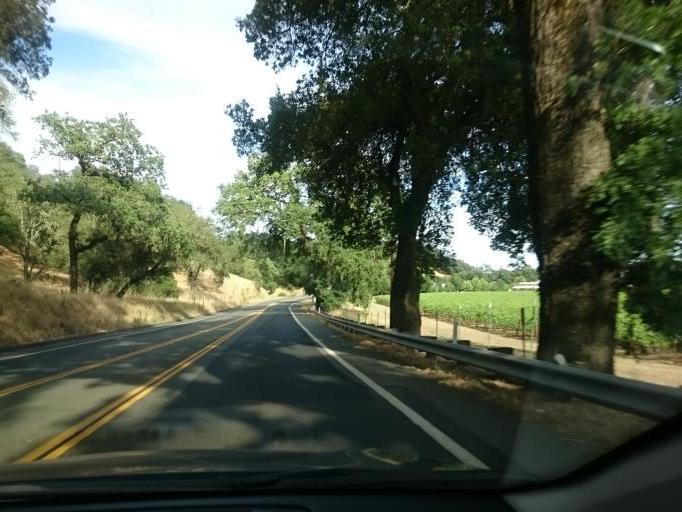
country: US
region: California
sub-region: Napa County
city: Saint Helena
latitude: 38.5056
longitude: -122.4386
